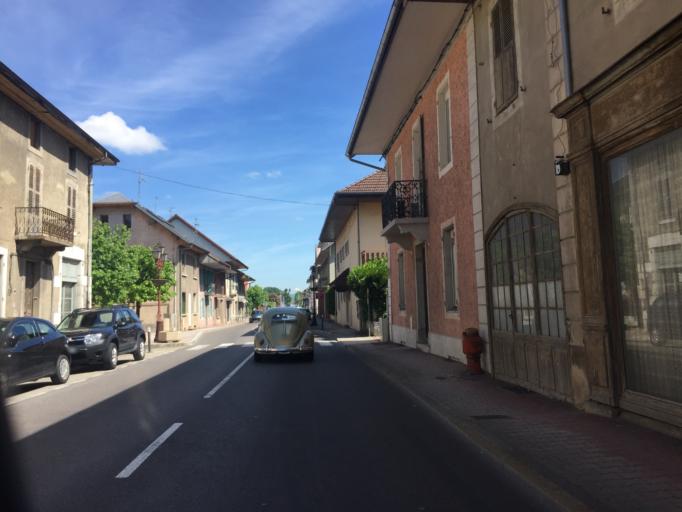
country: FR
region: Rhone-Alpes
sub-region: Departement de la Savoie
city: Albens
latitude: 45.7863
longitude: 5.9456
